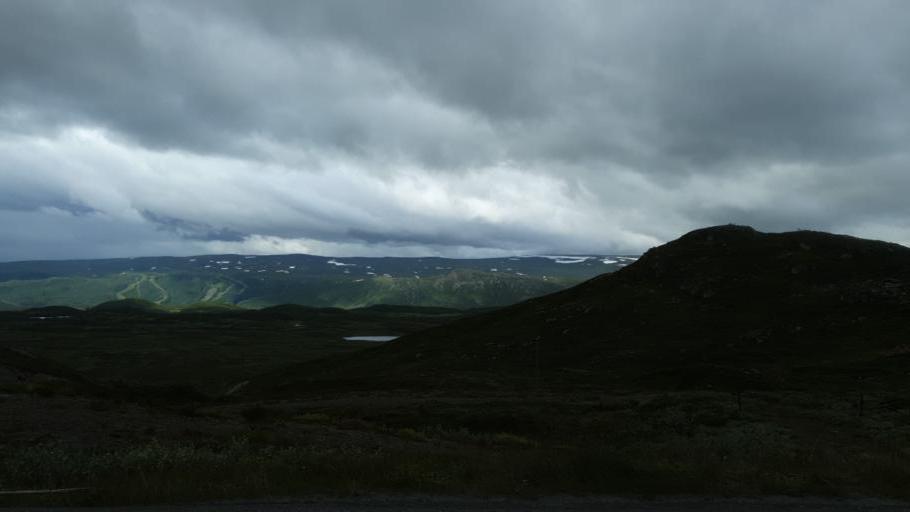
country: NO
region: Oppland
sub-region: Vestre Slidre
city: Slidre
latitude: 61.2818
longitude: 8.8378
